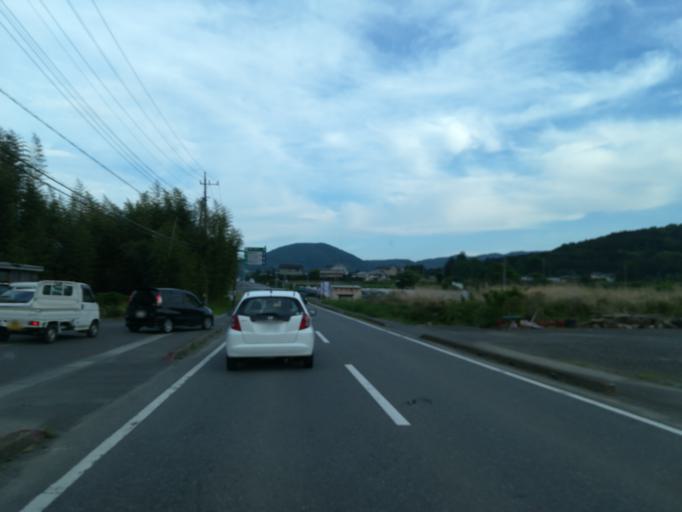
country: JP
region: Ibaraki
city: Tsukuba
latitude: 36.2120
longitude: 140.1745
